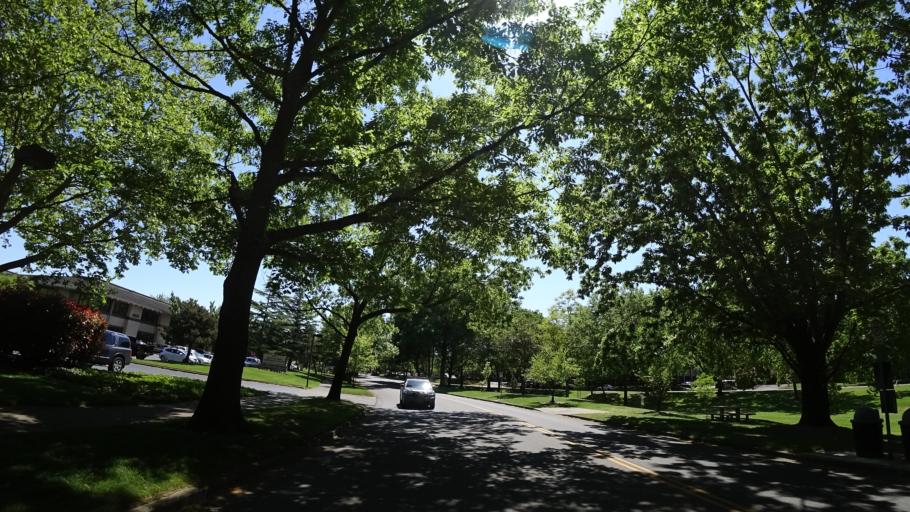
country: US
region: Oregon
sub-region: Washington County
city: Beaverton
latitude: 45.4850
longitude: -122.7954
